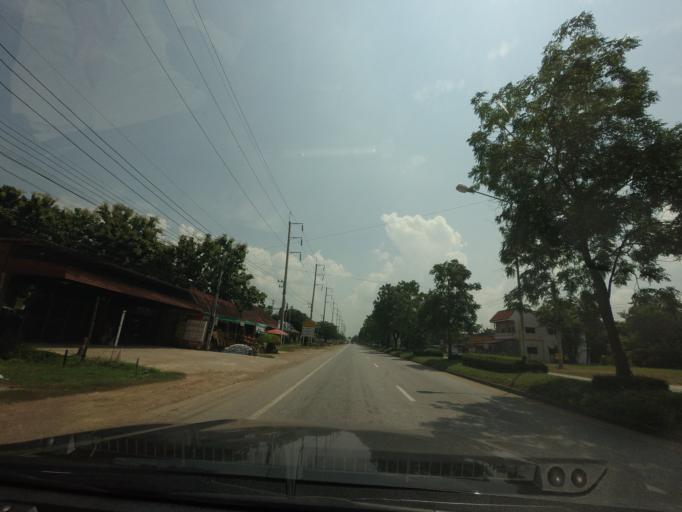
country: TH
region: Uttaradit
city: Uttaradit
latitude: 17.5911
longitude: 100.1331
